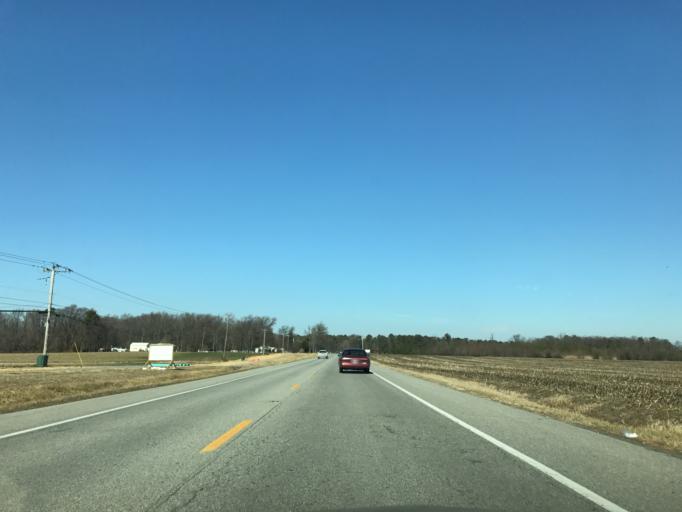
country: US
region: Maryland
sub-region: Queen Anne's County
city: Stevensville
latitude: 38.9272
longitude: -76.3549
